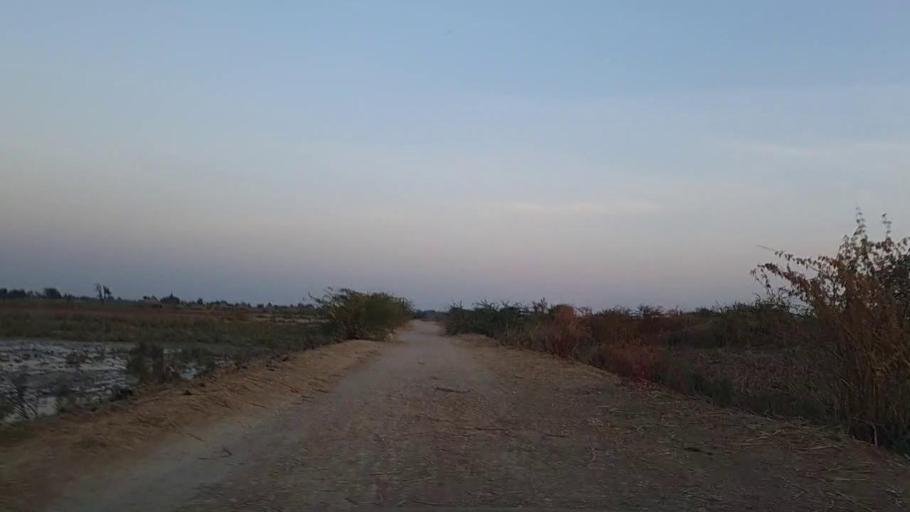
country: PK
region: Sindh
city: Tando Mittha Khan
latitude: 25.9406
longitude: 69.1425
